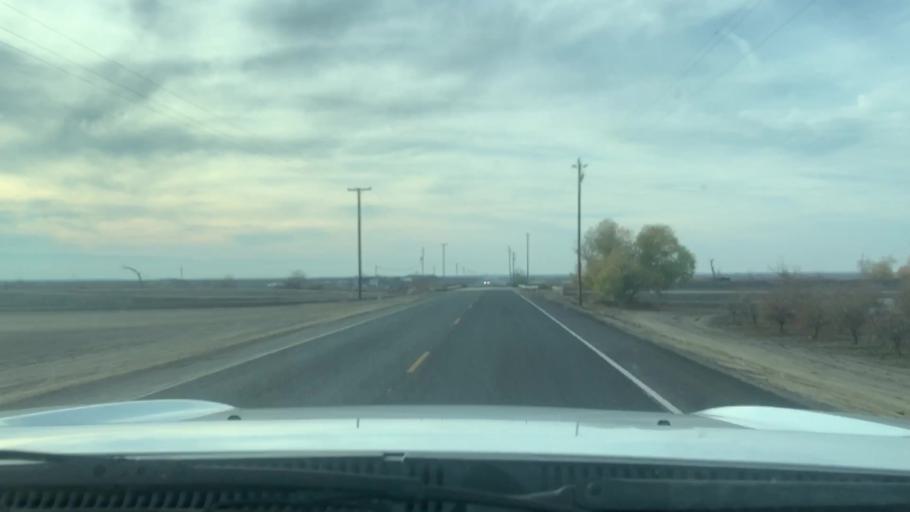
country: US
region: California
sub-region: Kern County
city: Lost Hills
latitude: 35.4995
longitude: -119.6169
